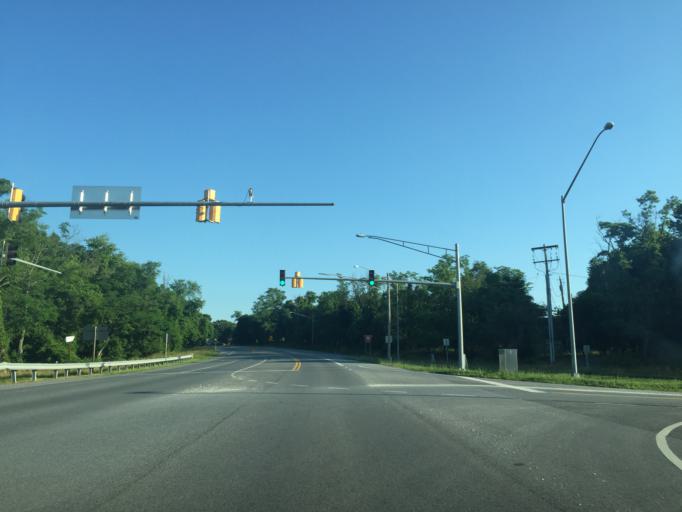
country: US
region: Maryland
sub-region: Baltimore County
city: Arbutus
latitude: 39.2471
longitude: -76.7204
